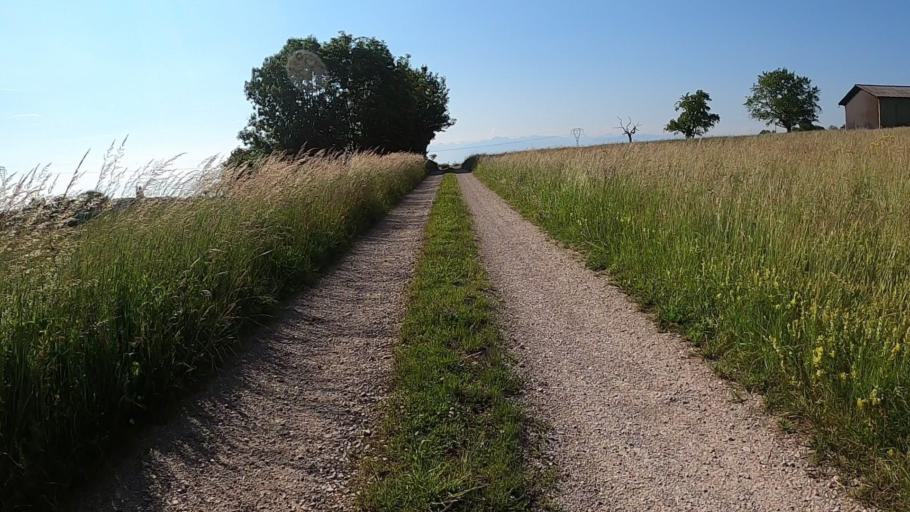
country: CH
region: Vaud
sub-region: Nyon District
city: Rolle
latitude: 46.4849
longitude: 6.3338
